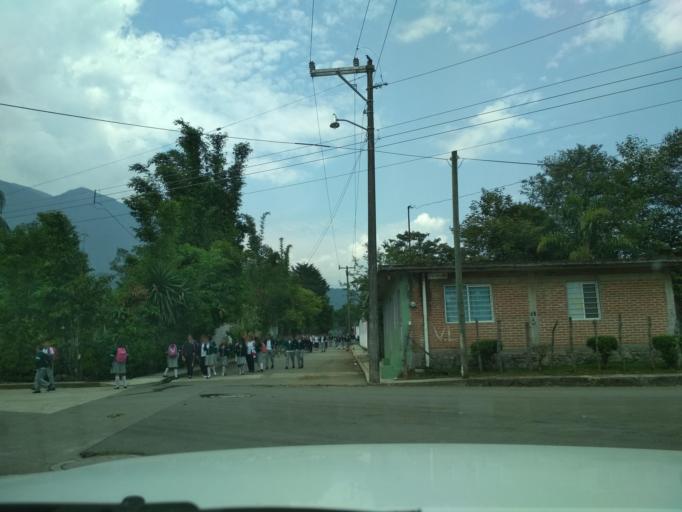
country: MX
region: Veracruz
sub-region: Mariano Escobedo
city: Mariano Escobedo
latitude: 18.9161
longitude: -97.1284
